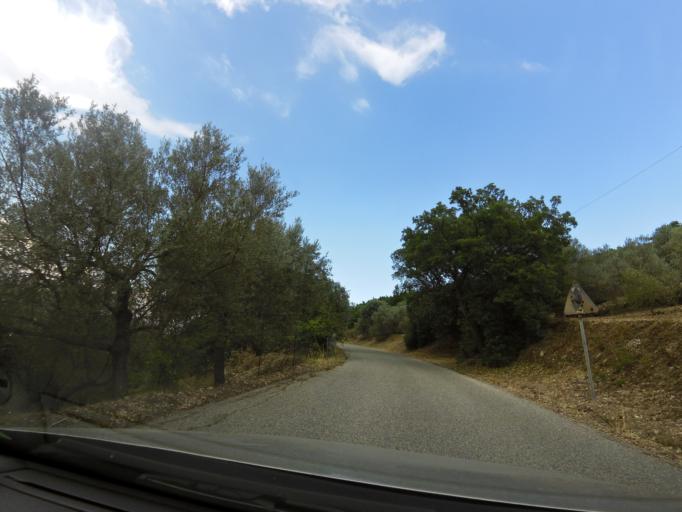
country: IT
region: Calabria
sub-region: Provincia di Reggio Calabria
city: Camini
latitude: 38.4327
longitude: 16.5028
